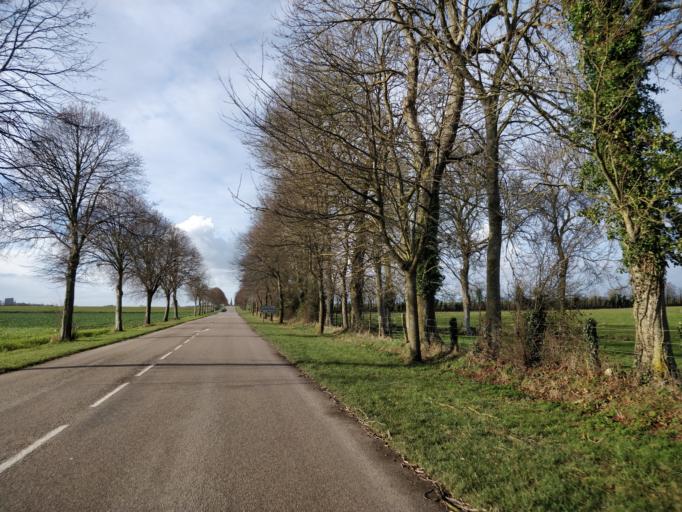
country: FR
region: Lower Normandy
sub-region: Departement du Calvados
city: Rots
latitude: 49.2032
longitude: -0.4879
